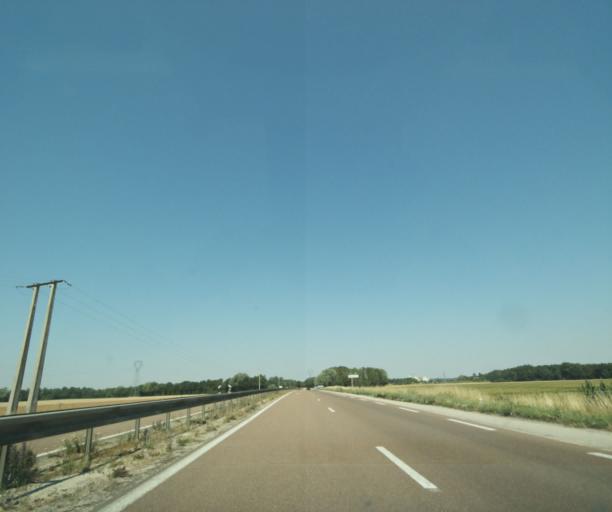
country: FR
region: Champagne-Ardenne
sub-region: Departement de la Marne
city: Frignicourt
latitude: 48.7090
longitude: 4.6484
